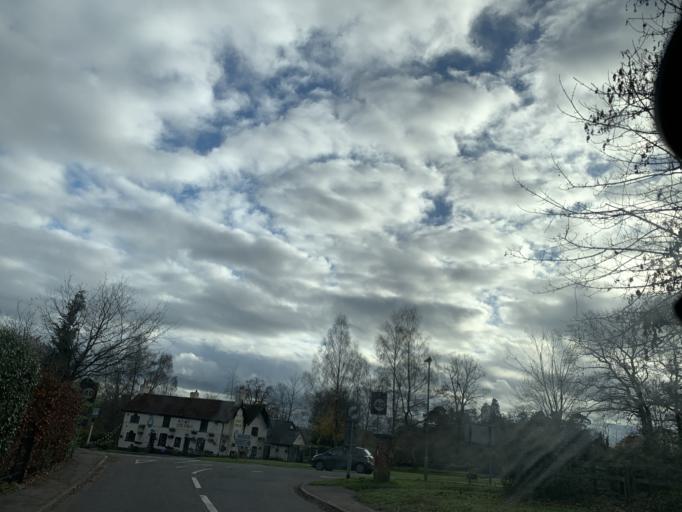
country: GB
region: England
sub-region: Hampshire
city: Lyndhurst
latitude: 50.8726
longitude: -1.5887
